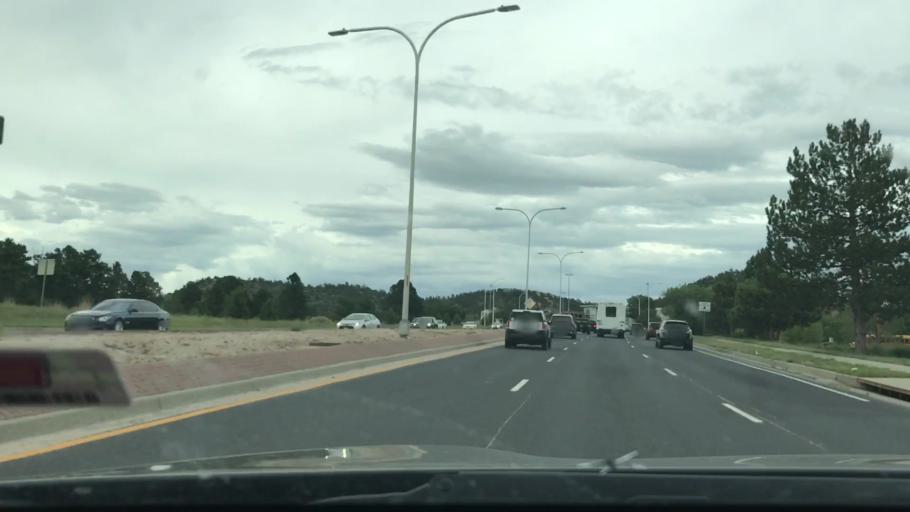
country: US
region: Colorado
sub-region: El Paso County
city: Colorado Springs
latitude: 38.8977
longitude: -104.8151
